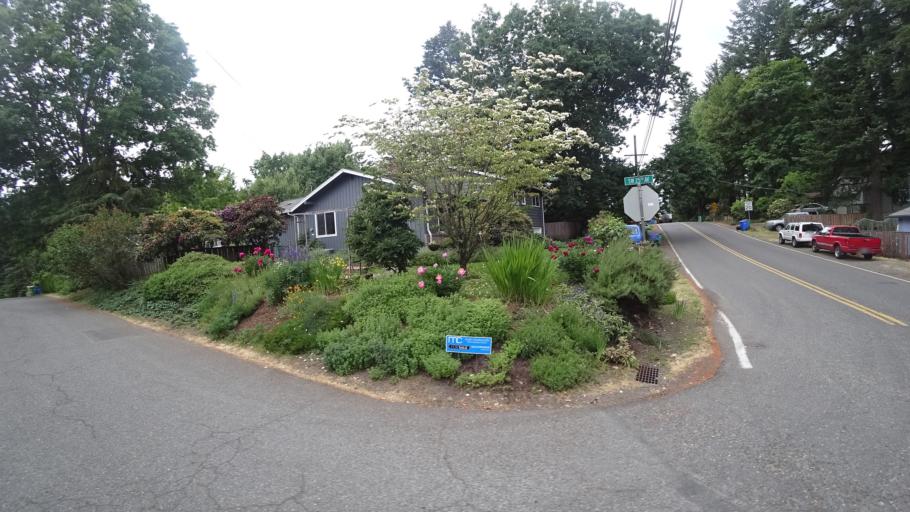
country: US
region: Oregon
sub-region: Clackamas County
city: Lake Oswego
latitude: 45.4517
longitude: -122.7025
